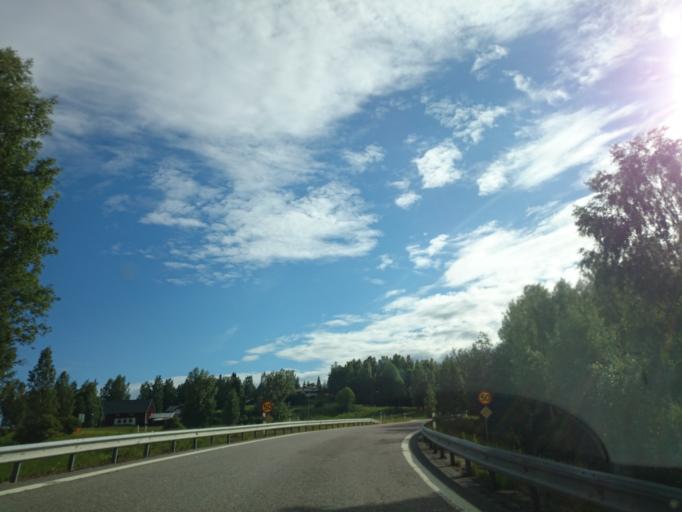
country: SE
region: Vaesternorrland
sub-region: Timra Kommun
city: Timra
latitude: 62.4782
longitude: 17.3136
